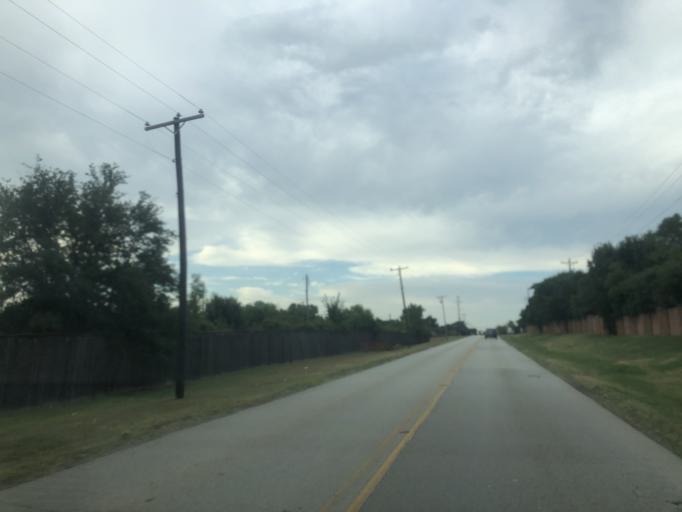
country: US
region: Texas
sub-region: Tarrant County
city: Southlake
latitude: 32.9477
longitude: -97.1511
